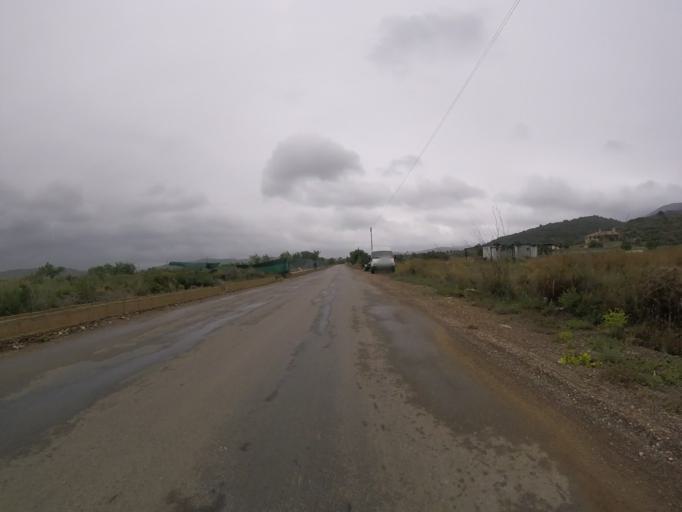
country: ES
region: Valencia
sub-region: Provincia de Castello
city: Alcoceber
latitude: 40.2445
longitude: 0.2479
